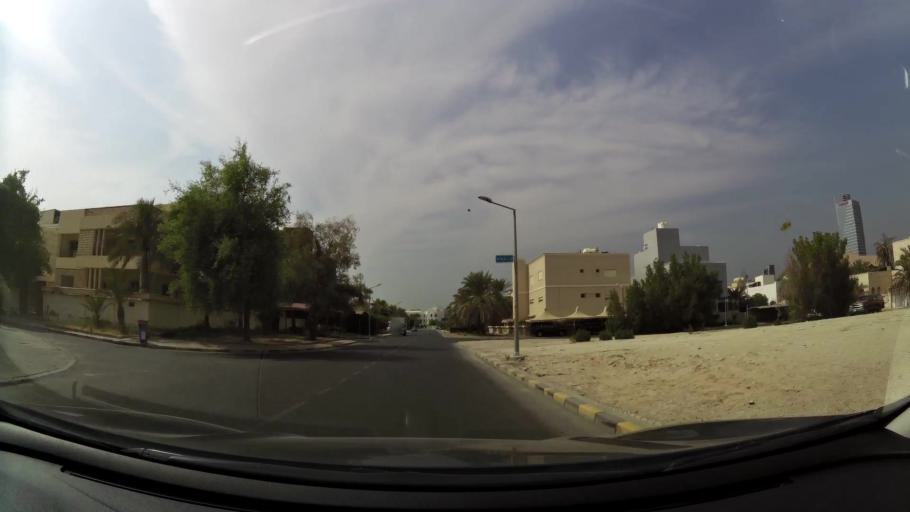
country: KW
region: Al Asimah
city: Kuwait City
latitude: 29.3571
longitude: 47.9797
